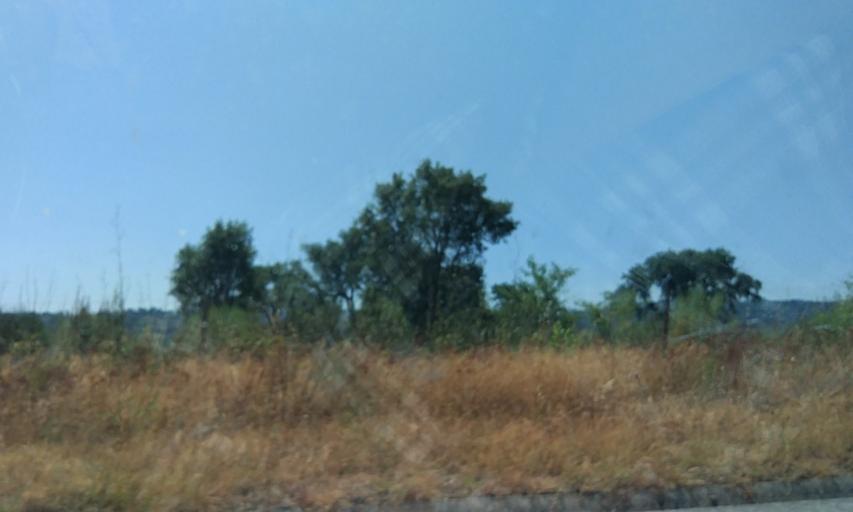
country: PT
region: Braganca
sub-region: Mirandela
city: Mirandela
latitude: 41.5252
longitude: -7.0972
